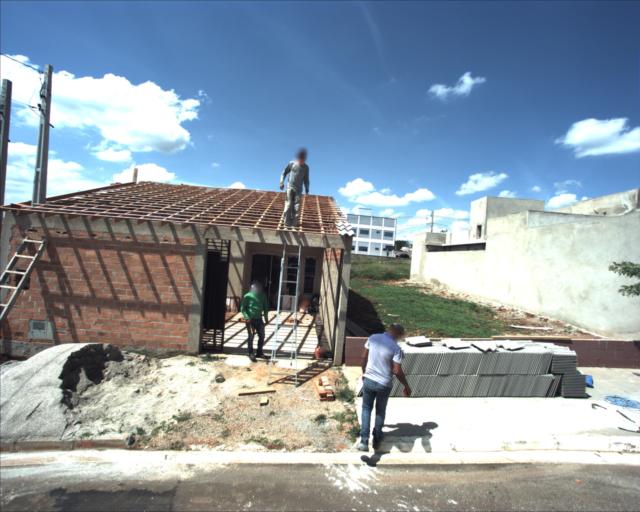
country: BR
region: Sao Paulo
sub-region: Sorocaba
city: Sorocaba
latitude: -23.4106
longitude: -47.4129
